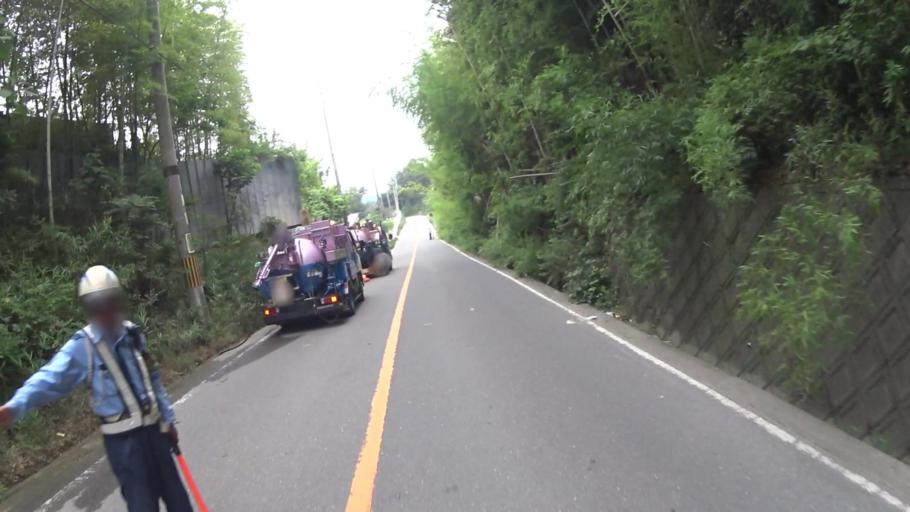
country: JP
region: Kyoto
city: Yawata
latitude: 34.8867
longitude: 135.7016
